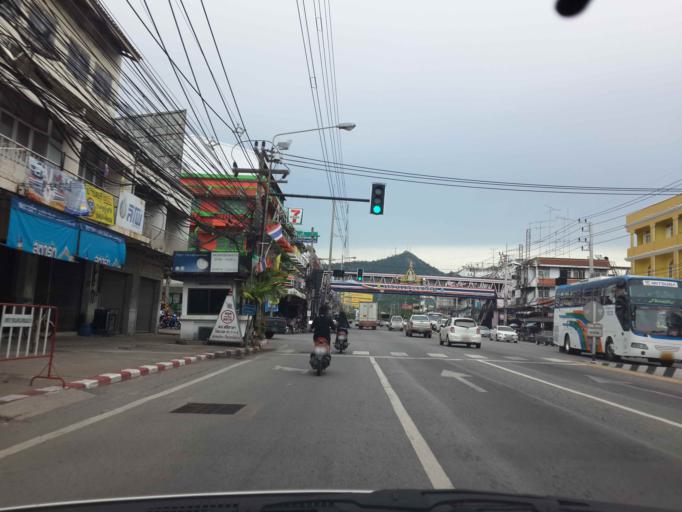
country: TH
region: Chon Buri
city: Si Racha
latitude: 13.2142
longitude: 100.9428
